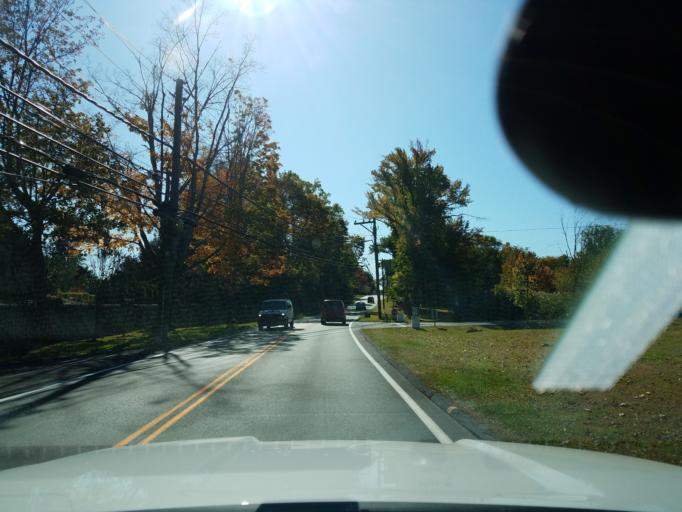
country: US
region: Connecticut
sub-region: Fairfield County
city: Cos Cob
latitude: 41.0702
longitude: -73.6225
